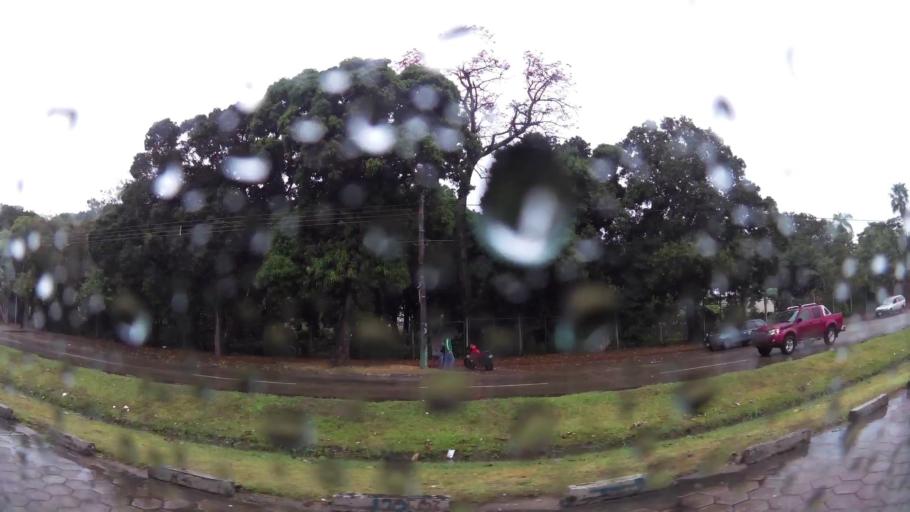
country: BO
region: Santa Cruz
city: Santa Cruz de la Sierra
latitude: -17.7912
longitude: -63.2128
